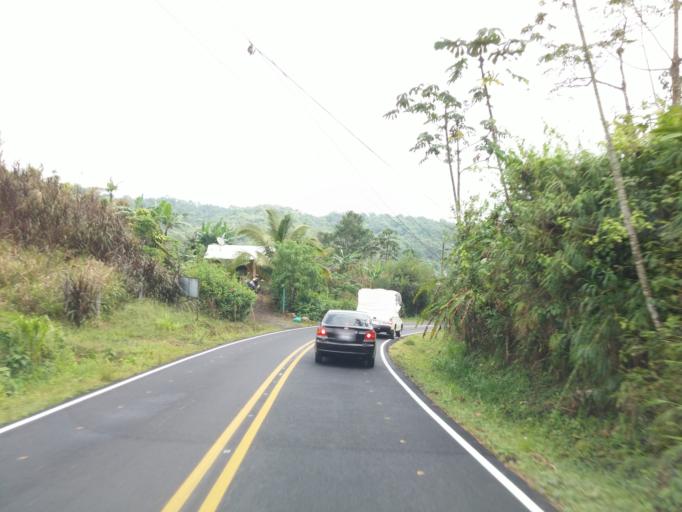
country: CR
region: Alajuela
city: San Ramon
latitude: 10.2145
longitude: -84.5426
